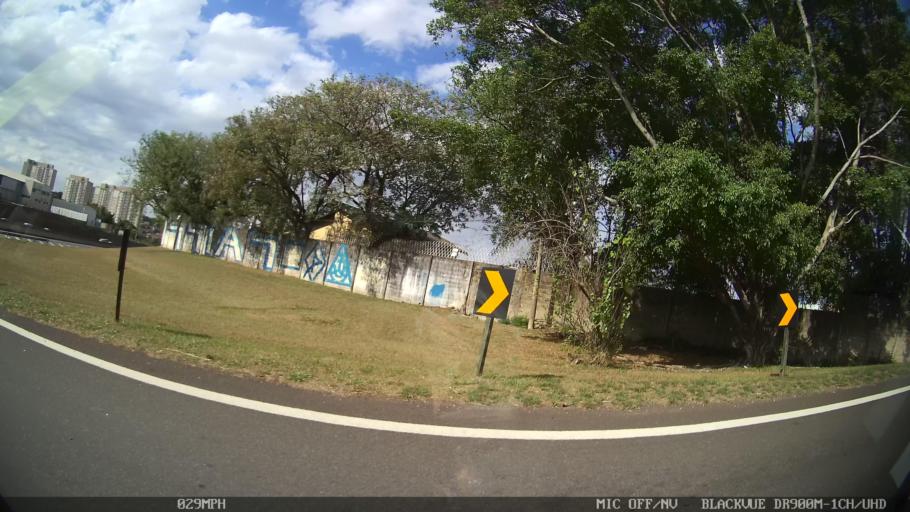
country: BR
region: Sao Paulo
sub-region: Limeira
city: Limeira
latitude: -22.5672
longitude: -47.4375
